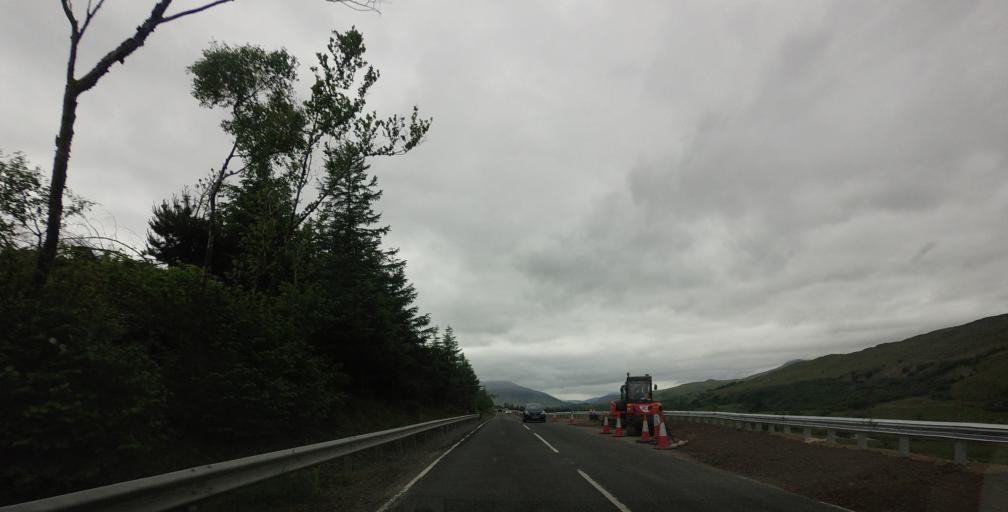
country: GB
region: Scotland
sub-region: Stirling
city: Callander
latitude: 56.4398
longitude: -4.3651
